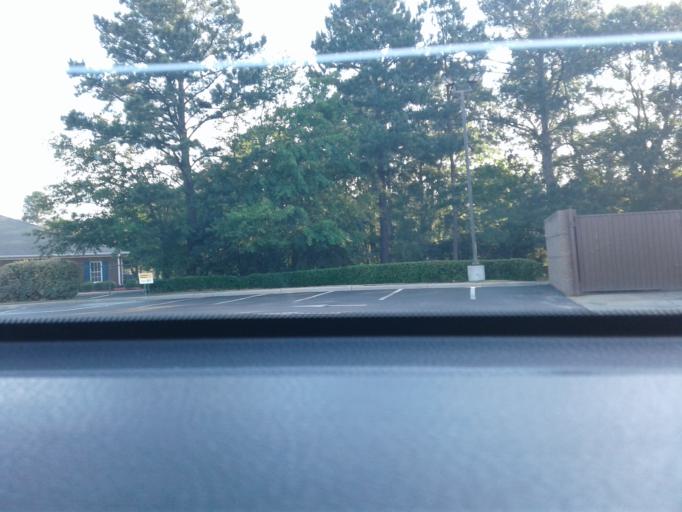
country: US
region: North Carolina
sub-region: Harnett County
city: Dunn
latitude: 35.3174
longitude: -78.6267
